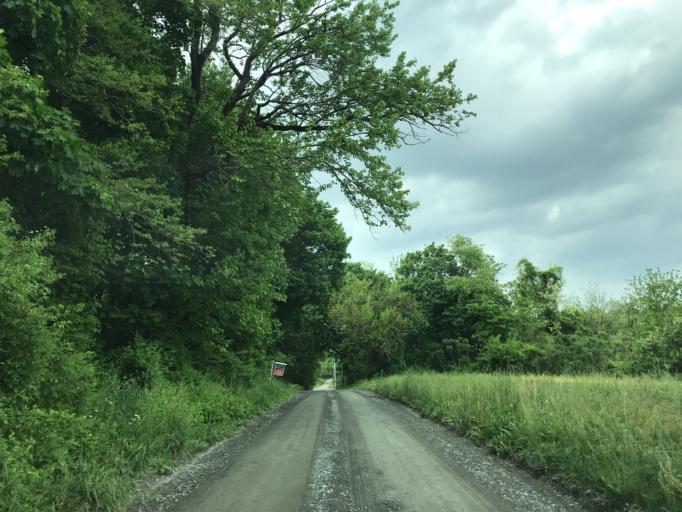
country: US
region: Pennsylvania
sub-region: York County
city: Susquehanna Trails
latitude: 39.7035
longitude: -76.3413
